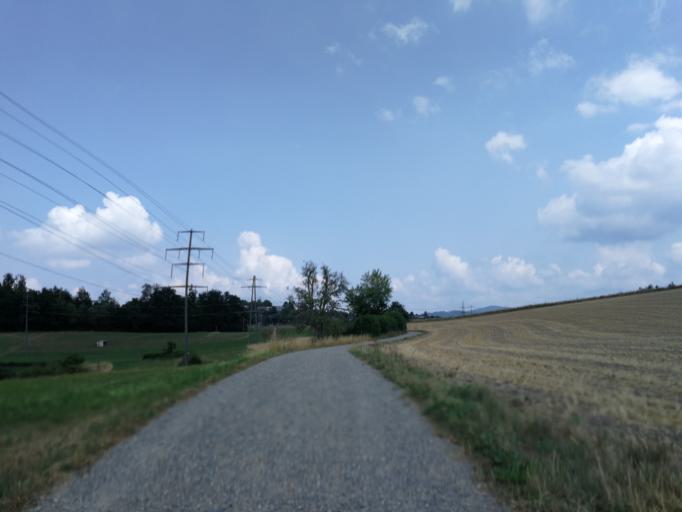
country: CH
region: Zurich
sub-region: Bezirk Hinwil
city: Gossau
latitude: 47.3255
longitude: 8.7525
